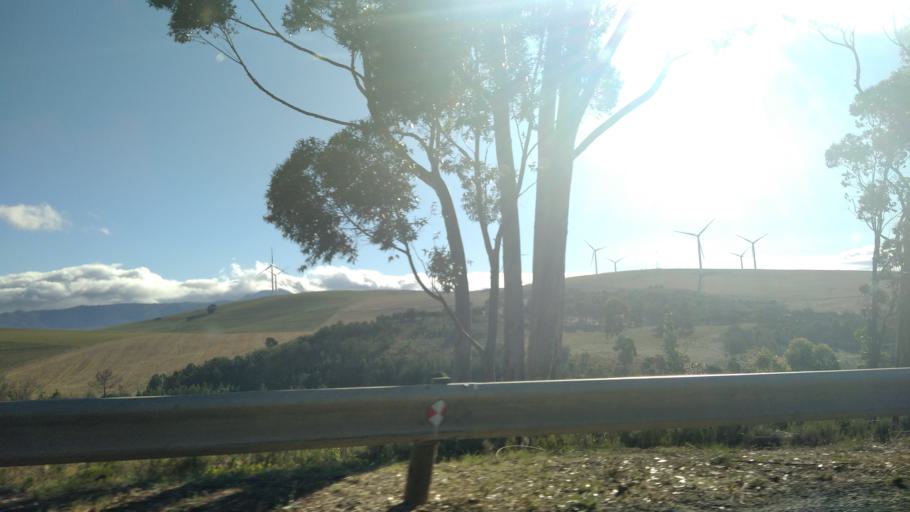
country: ZA
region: Western Cape
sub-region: Overberg District Municipality
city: Caledon
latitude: -34.2210
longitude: 19.4063
